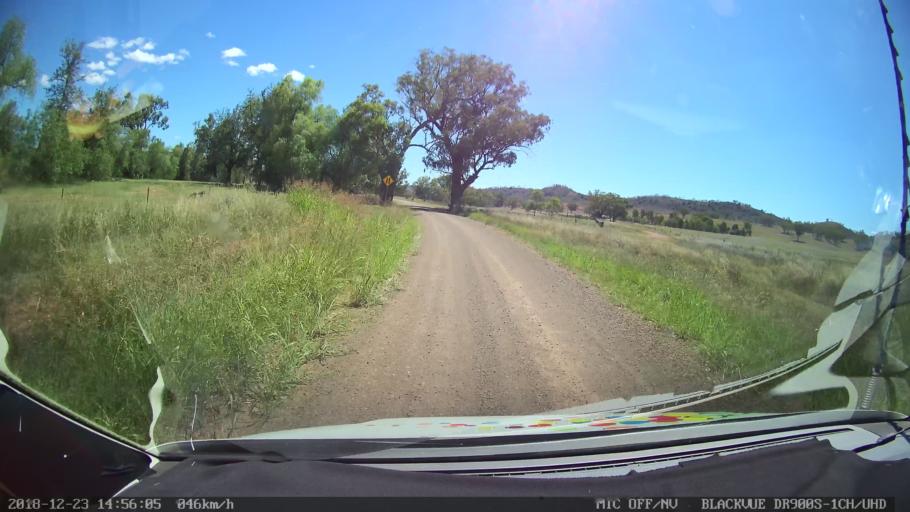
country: AU
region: New South Wales
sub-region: Tamworth Municipality
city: Manilla
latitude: -30.7024
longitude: 150.8311
